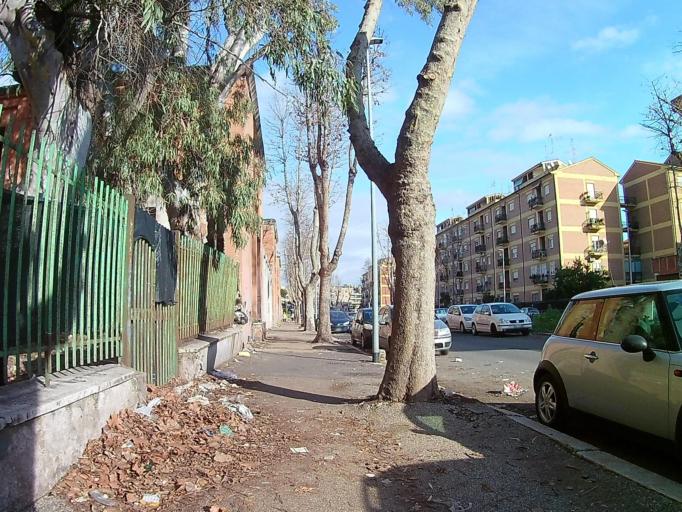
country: IT
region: Latium
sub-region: Citta metropolitana di Roma Capitale
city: Lido di Ostia
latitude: 41.7342
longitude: 12.2714
